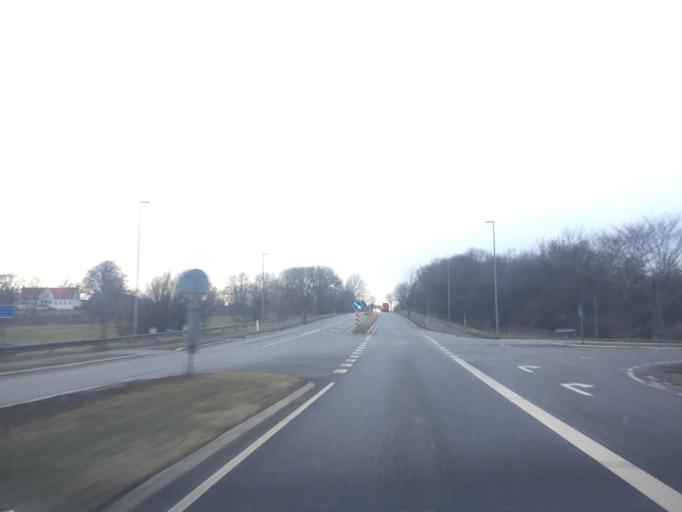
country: DK
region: Zealand
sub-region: Solrod Kommune
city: Solrod Strand
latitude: 55.5655
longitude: 12.2255
